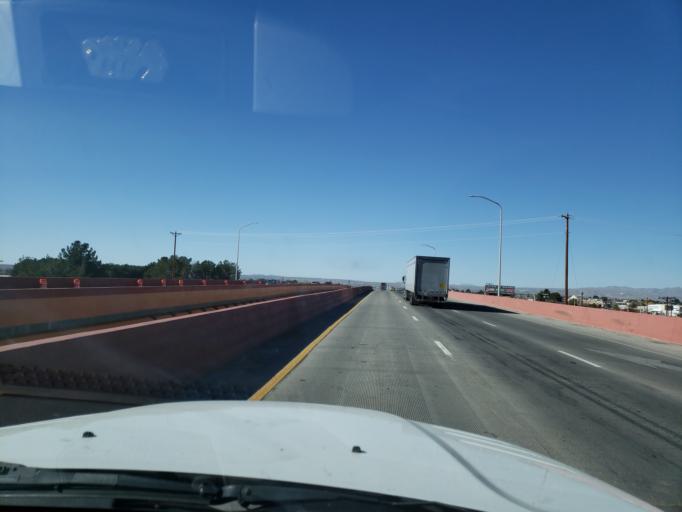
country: US
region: New Mexico
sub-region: Dona Ana County
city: University Park
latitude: 32.2810
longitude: -106.7694
